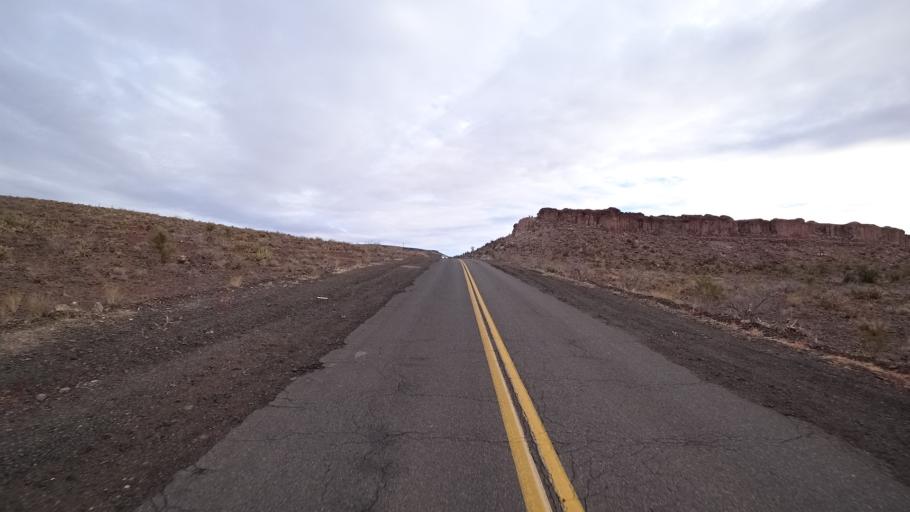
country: US
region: Arizona
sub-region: Mohave County
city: Kingman
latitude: 35.2097
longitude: -114.0793
